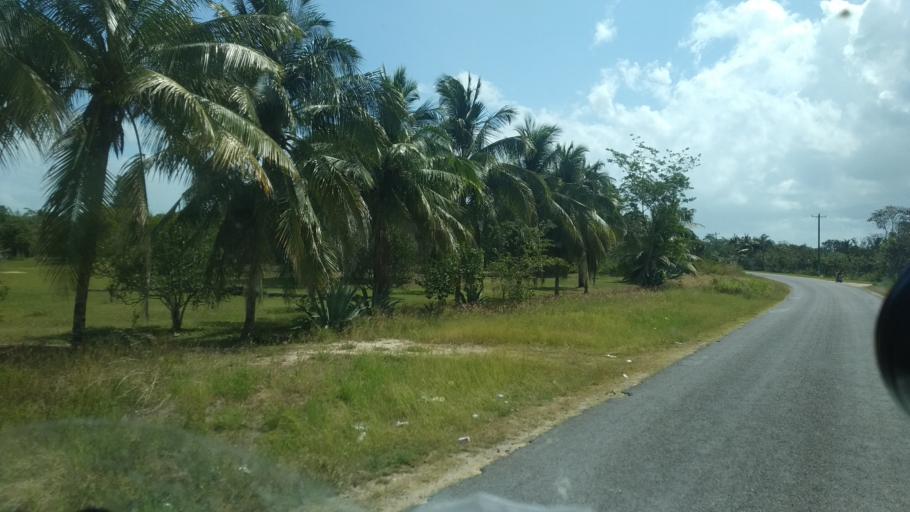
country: BZ
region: Corozal
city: Corozal
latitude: 18.3905
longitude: -88.4208
